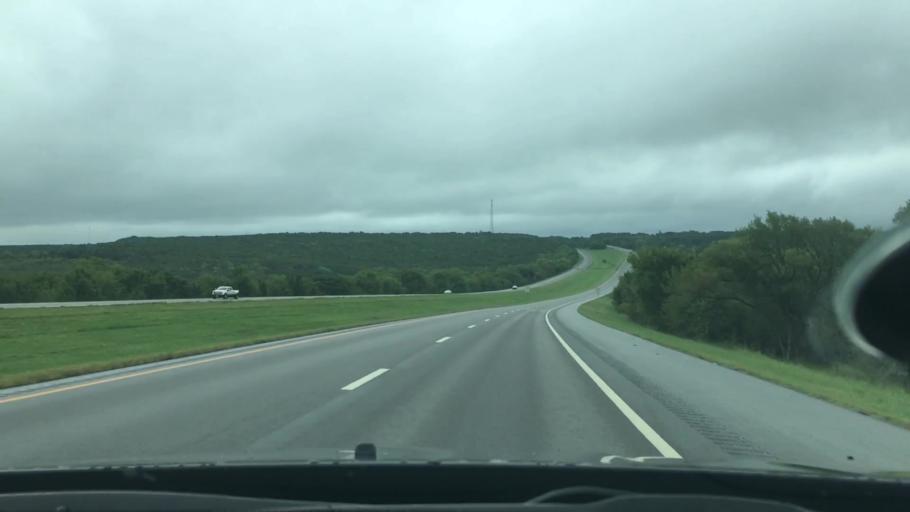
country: US
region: Oklahoma
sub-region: Okmulgee County
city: Henryetta
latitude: 35.4364
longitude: -95.8258
